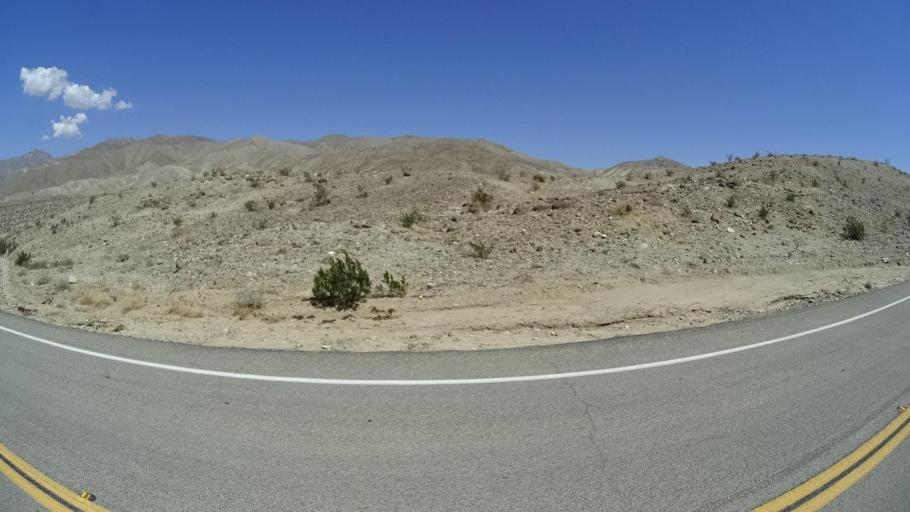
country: US
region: California
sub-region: Imperial County
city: Desert Shores
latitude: 33.2892
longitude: -116.1678
